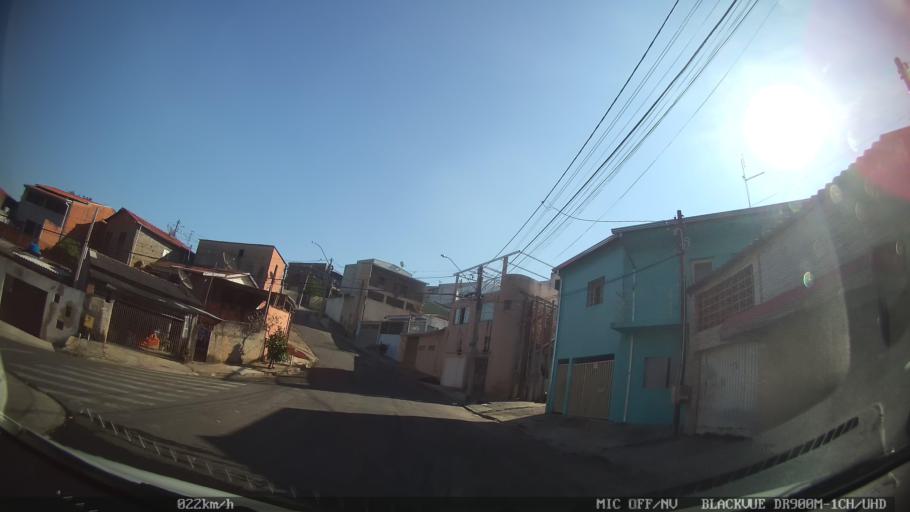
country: BR
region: Sao Paulo
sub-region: Campinas
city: Campinas
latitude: -22.9569
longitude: -47.0918
